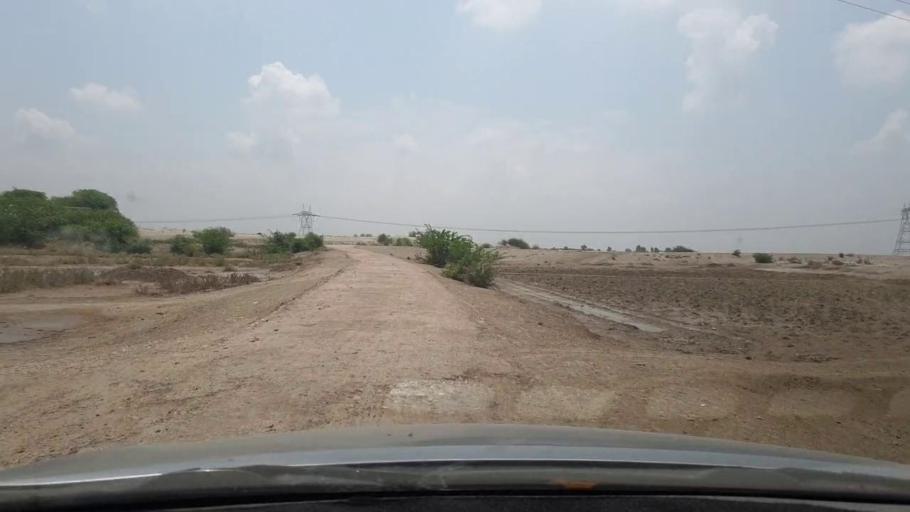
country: PK
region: Sindh
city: Khairpur
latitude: 27.4536
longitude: 68.7214
